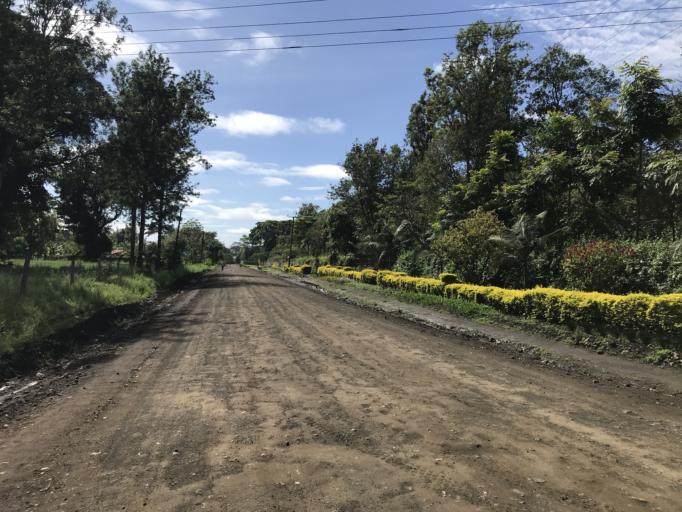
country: TZ
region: Arusha
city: Nkoaranga
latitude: -3.3799
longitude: 36.7927
